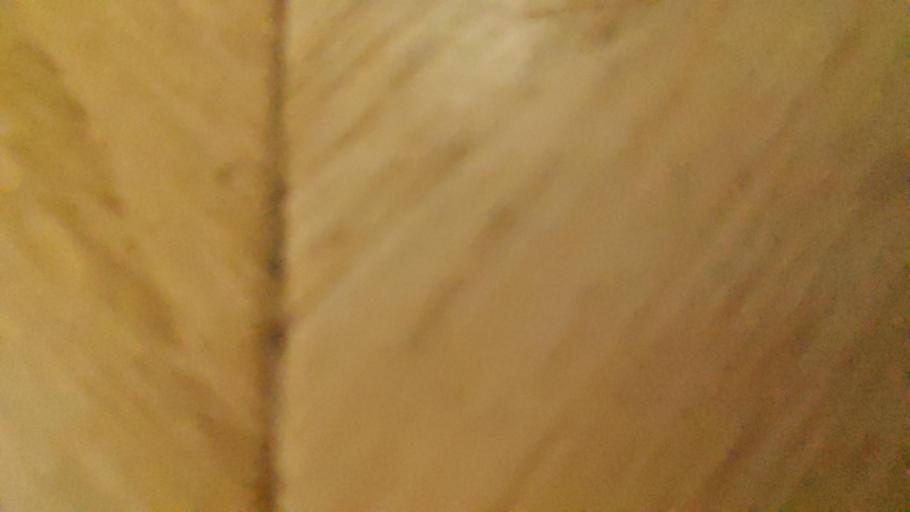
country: US
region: Colorado
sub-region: Weld County
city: Lochbuie
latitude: 39.9837
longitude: -104.7495
